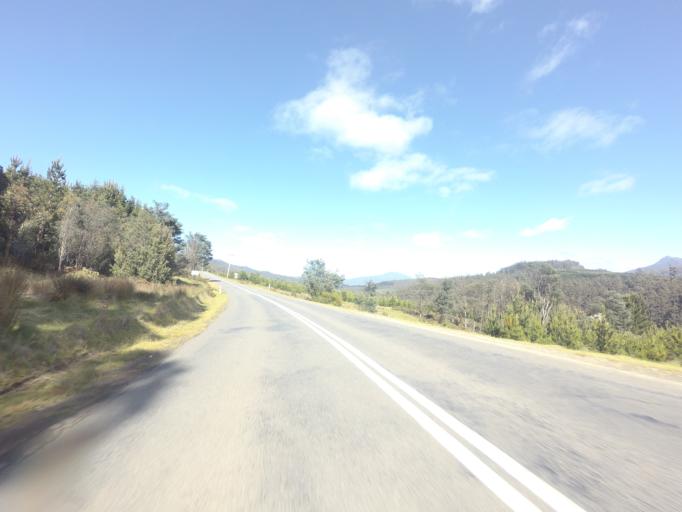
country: AU
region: Tasmania
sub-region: Derwent Valley
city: New Norfolk
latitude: -42.7409
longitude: 146.6590
